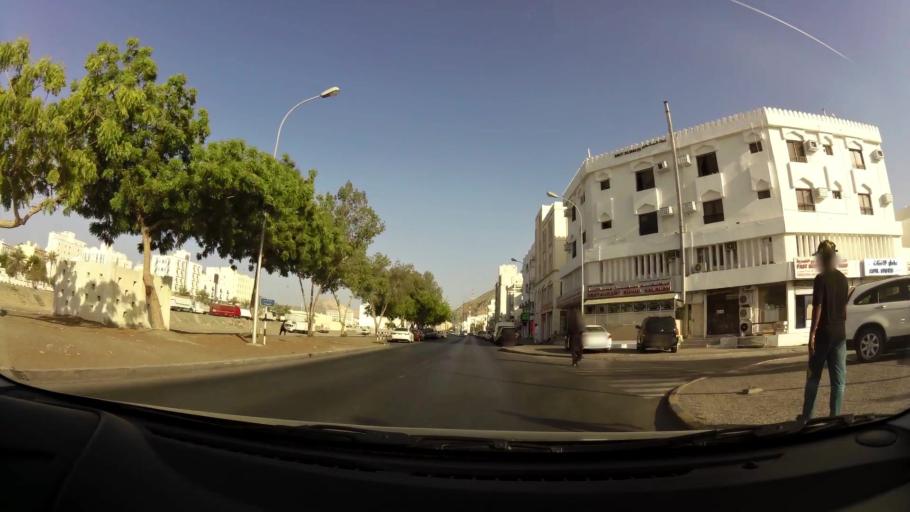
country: OM
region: Muhafazat Masqat
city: Muscat
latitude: 23.5907
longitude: 58.5502
